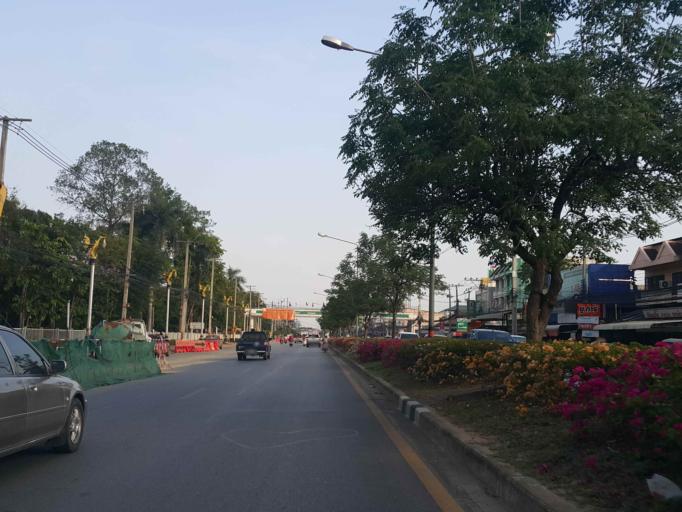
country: TH
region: Chiang Mai
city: San Sai
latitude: 18.8966
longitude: 99.0084
